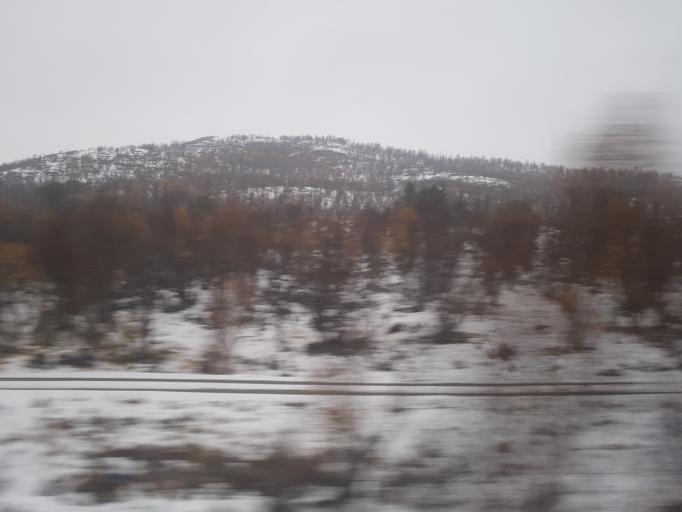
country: NO
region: Oppland
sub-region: Dovre
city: Dovre
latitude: 62.1765
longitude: 9.4522
